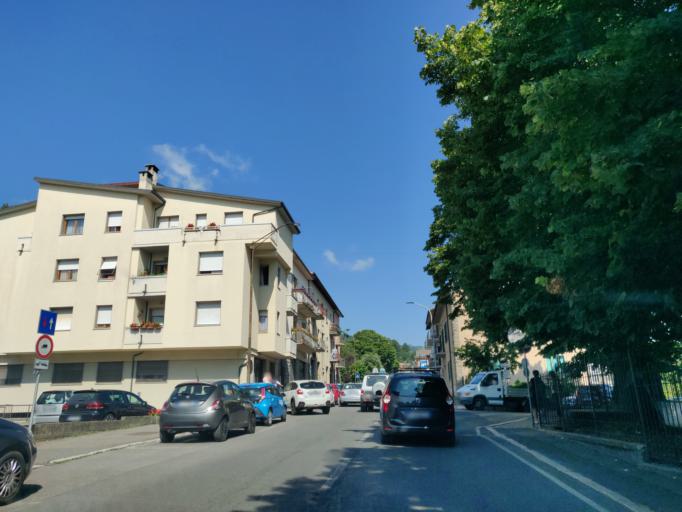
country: IT
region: Tuscany
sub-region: Provincia di Siena
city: Abbadia San Salvatore
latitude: 42.8821
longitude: 11.6734
